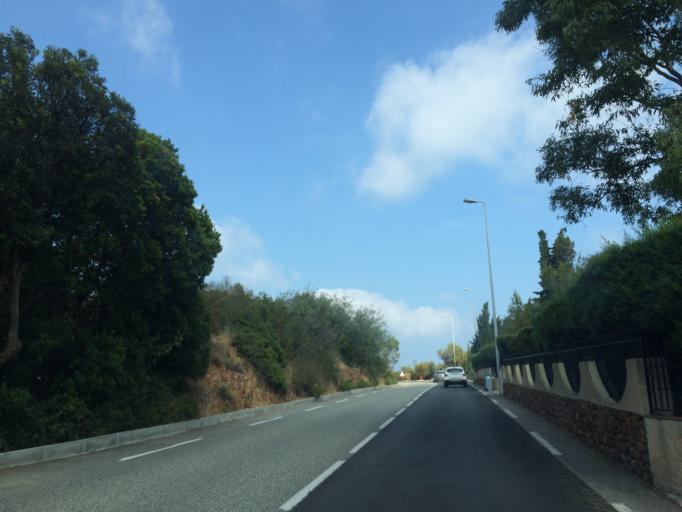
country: FR
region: Provence-Alpes-Cote d'Azur
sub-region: Departement des Alpes-Maritimes
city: Theoule-sur-Mer
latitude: 43.4406
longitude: 6.8970
